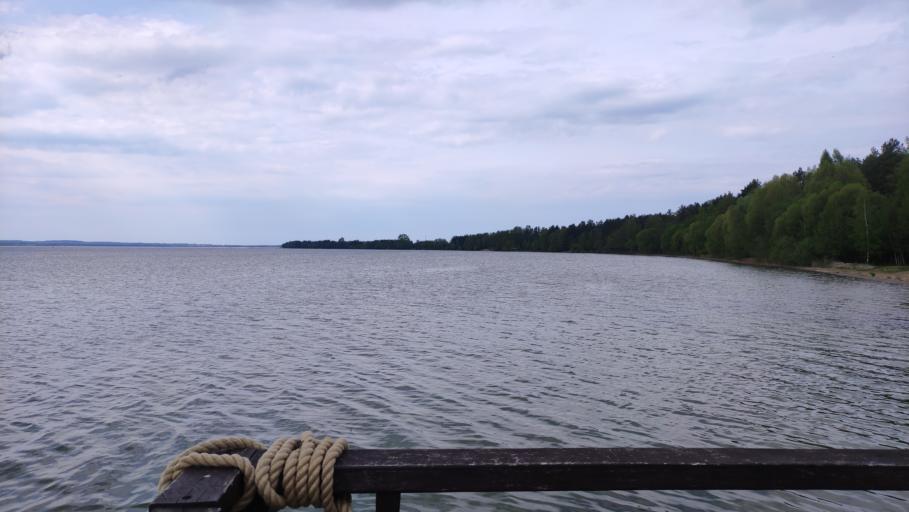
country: LT
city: Simnas
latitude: 54.2833
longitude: 23.7401
